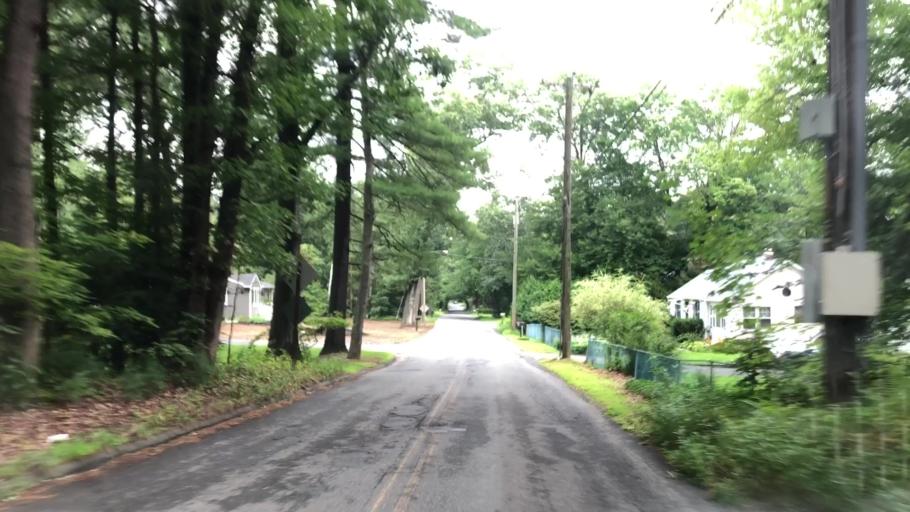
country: US
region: Massachusetts
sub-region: Hampshire County
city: Easthampton
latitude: 42.2829
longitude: -72.7140
